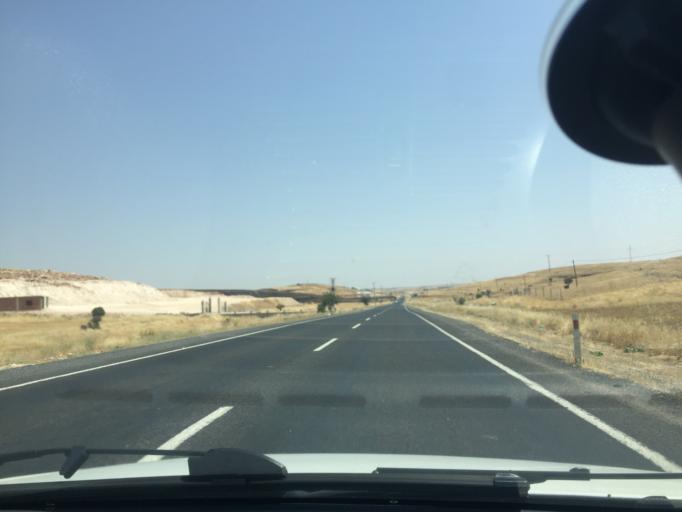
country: TR
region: Mardin
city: Kindirip
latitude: 37.4626
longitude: 41.2306
